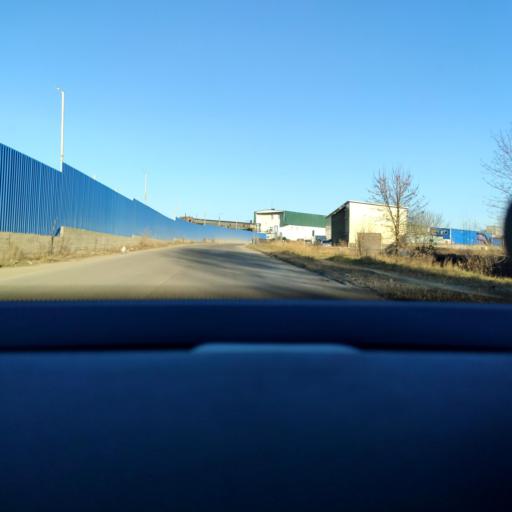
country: RU
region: Moskovskaya
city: Kotel'niki
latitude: 55.6339
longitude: 37.8254
